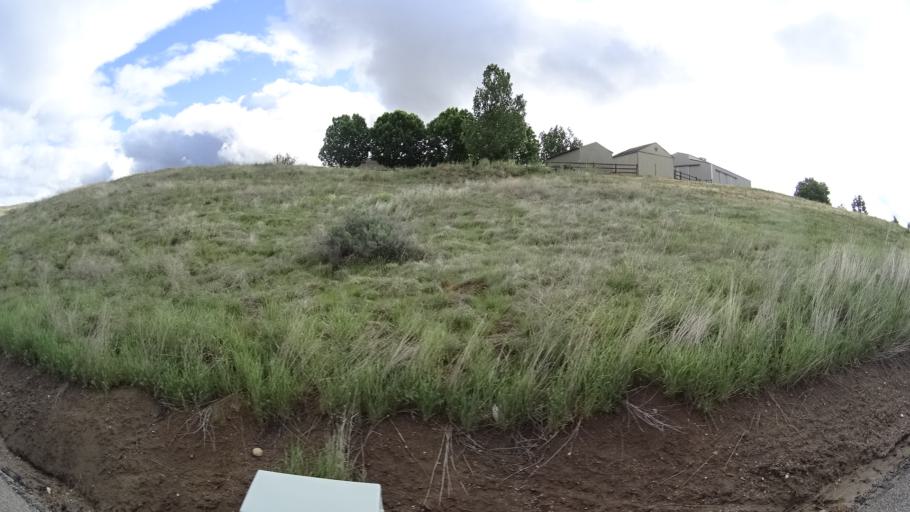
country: US
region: Idaho
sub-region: Ada County
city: Eagle
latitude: 43.7271
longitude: -116.2650
